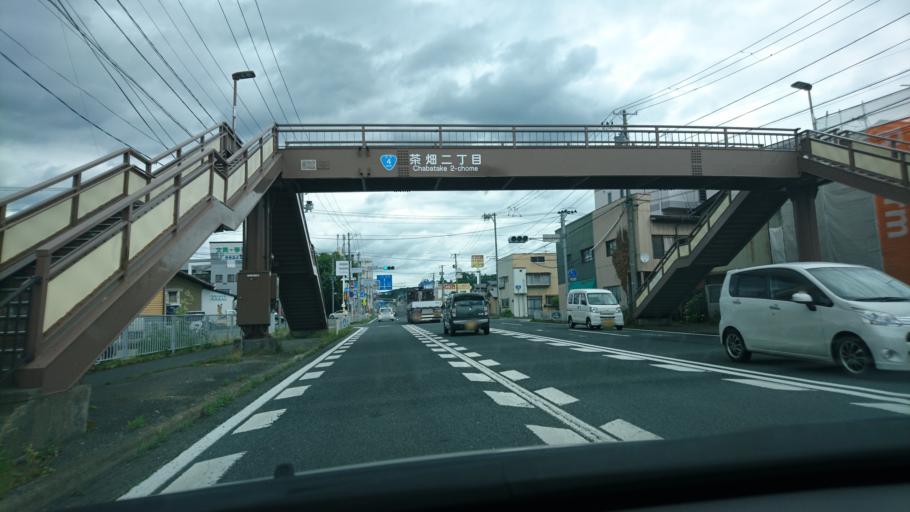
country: JP
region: Iwate
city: Morioka-shi
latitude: 39.6914
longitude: 141.1659
